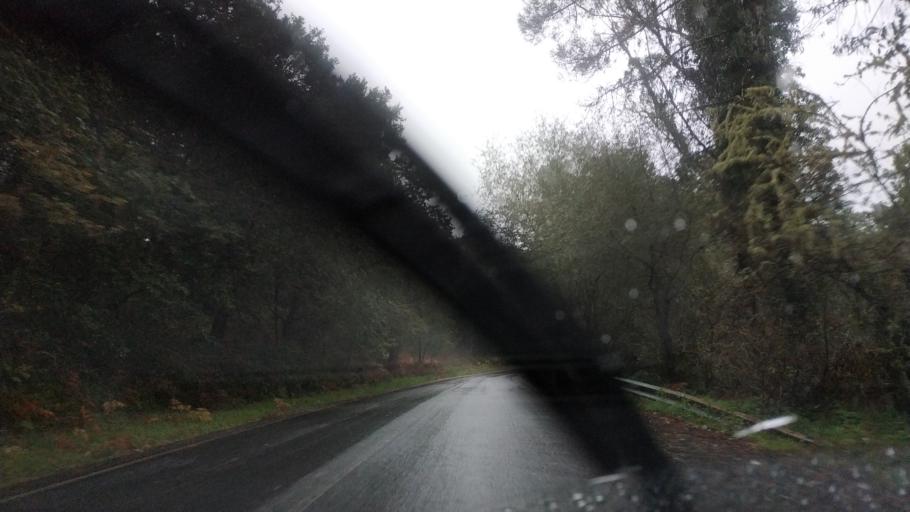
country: ES
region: Galicia
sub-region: Provincia da Coruna
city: Negreira
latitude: 42.9074
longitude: -8.7471
